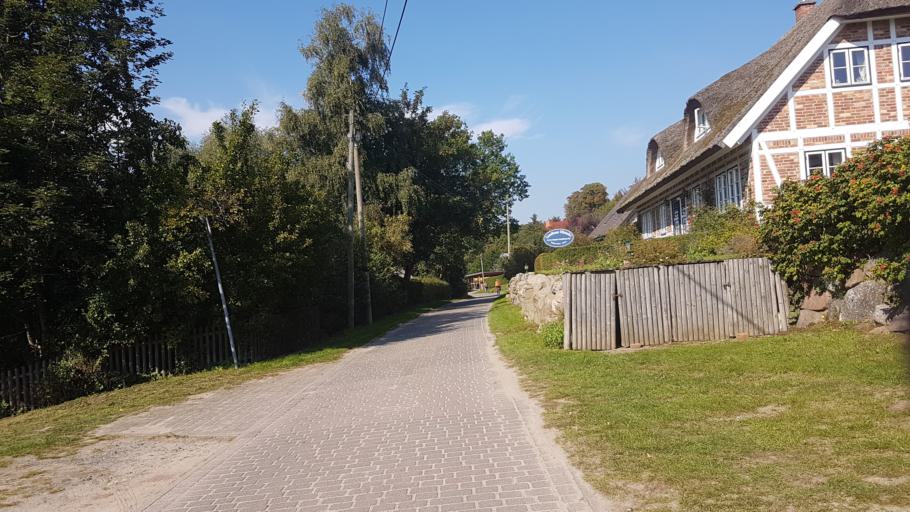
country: DE
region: Mecklenburg-Vorpommern
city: Putbus
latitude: 54.3540
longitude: 13.5220
